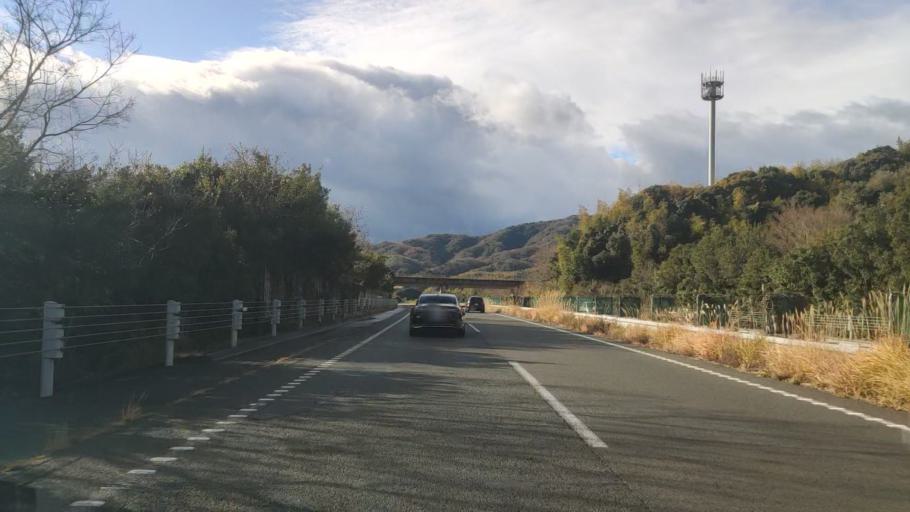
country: JP
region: Hyogo
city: Sumoto
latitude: 34.3971
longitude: 134.8610
